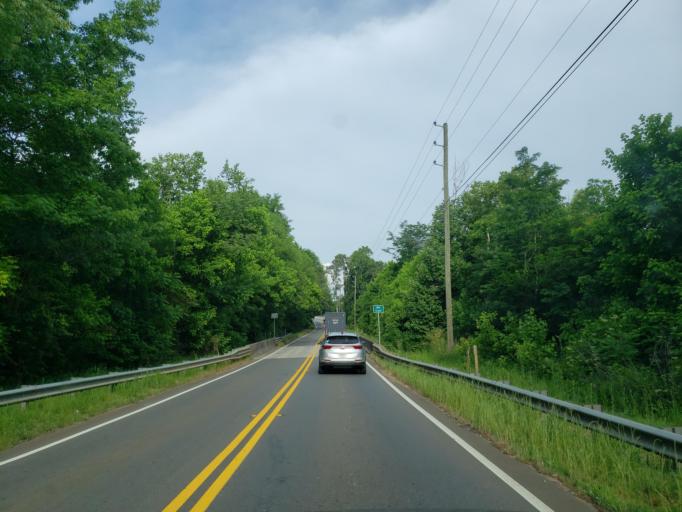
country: US
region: Georgia
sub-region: Cherokee County
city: Holly Springs
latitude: 34.1699
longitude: -84.3992
